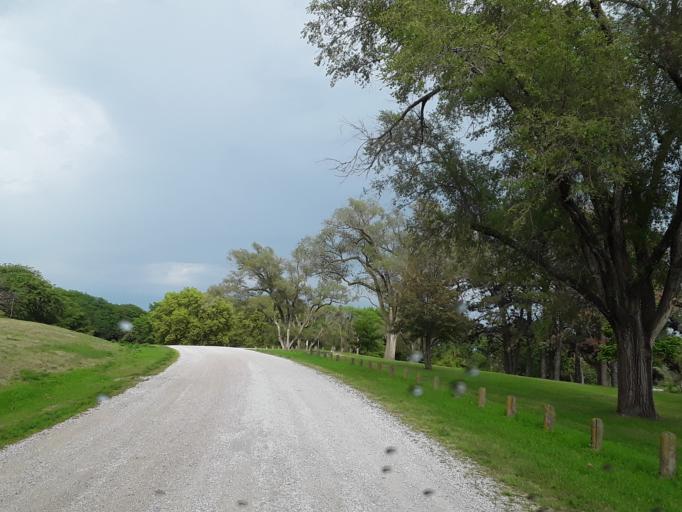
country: US
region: Nebraska
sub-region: Saunders County
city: Ashland
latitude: 41.1021
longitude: -96.4431
